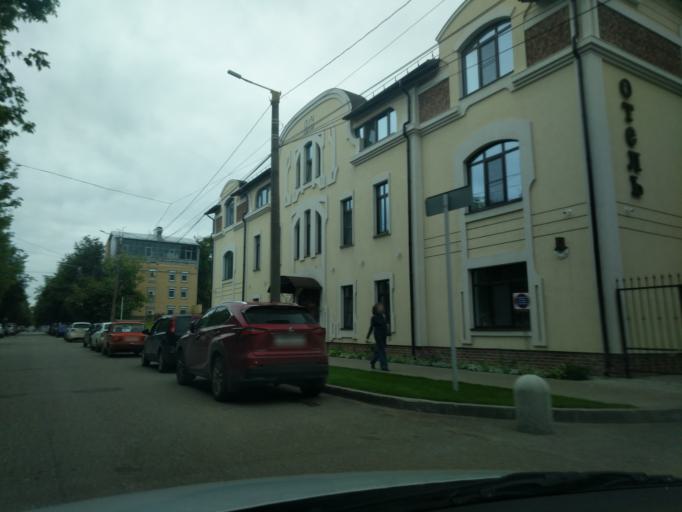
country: RU
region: Kirov
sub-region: Kirovo-Chepetskiy Rayon
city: Kirov
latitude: 58.5961
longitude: 49.6705
